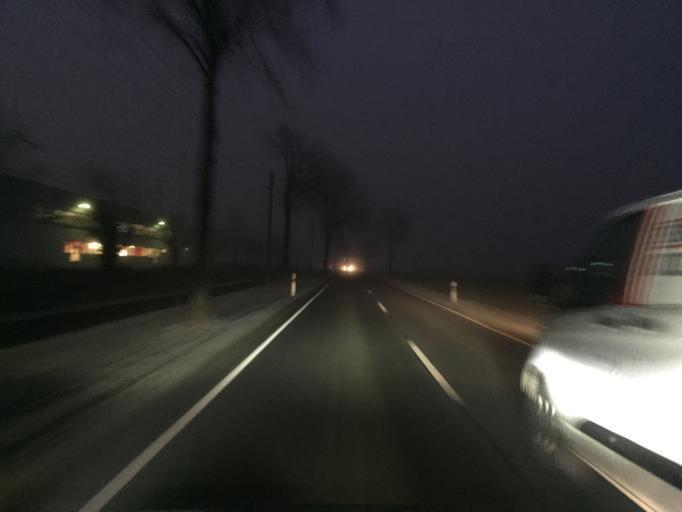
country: DE
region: Lower Saxony
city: Borstel
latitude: 52.6048
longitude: 8.9202
